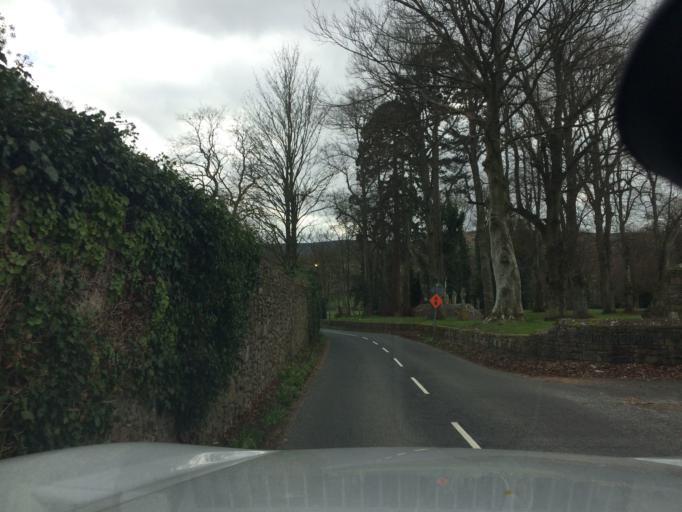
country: IE
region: Munster
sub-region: South Tipperary
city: Cluain Meala
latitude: 52.3587
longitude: -7.6508
